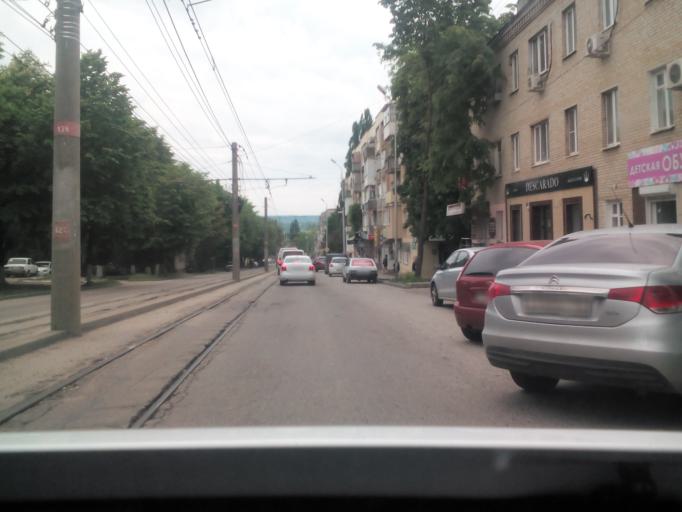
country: RU
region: Stavropol'skiy
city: Pyatigorsk
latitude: 44.0488
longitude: 43.0632
